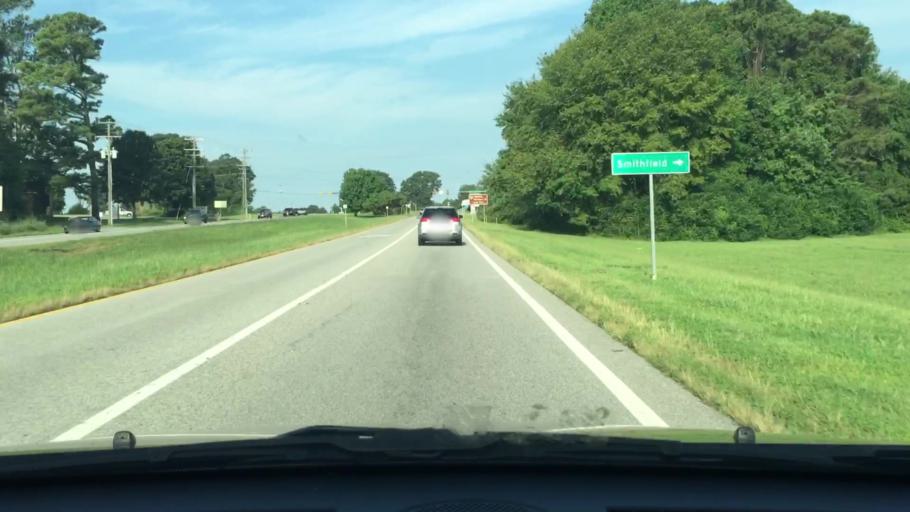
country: US
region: Virginia
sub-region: Isle of Wight County
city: Carrollton
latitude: 36.9380
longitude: -76.5838
